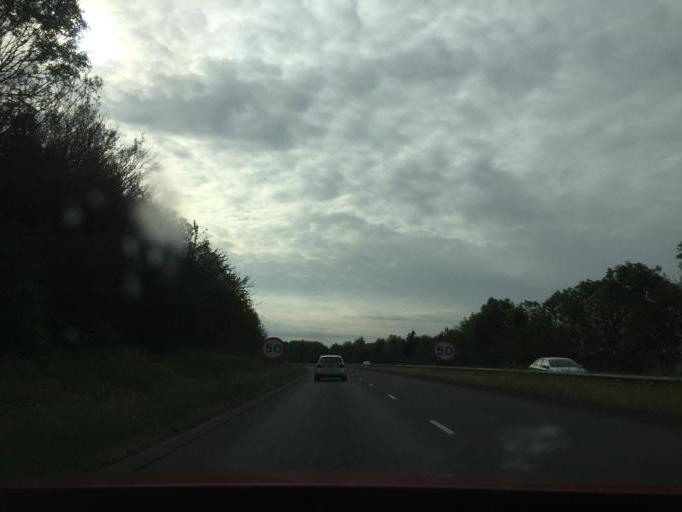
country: GB
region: England
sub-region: Leicestershire
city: Lutterworth
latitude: 52.4513
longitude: -1.2173
